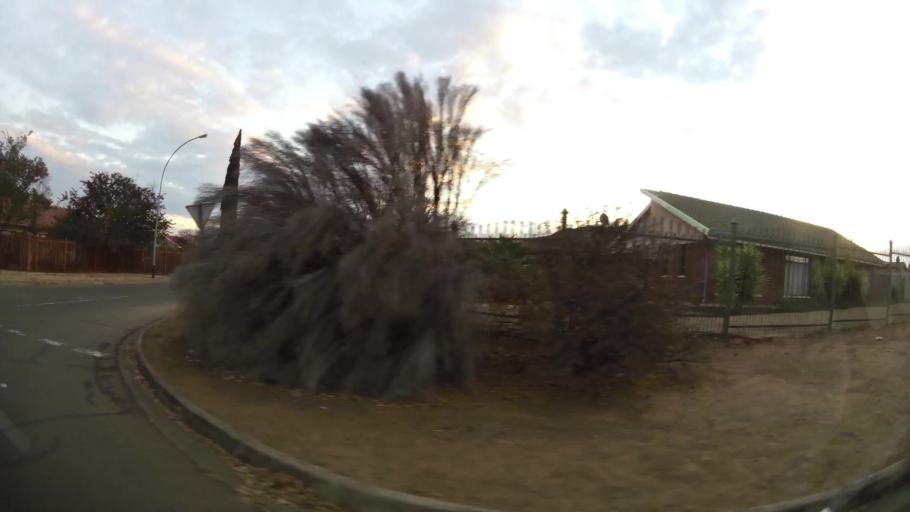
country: ZA
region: Orange Free State
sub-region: Mangaung Metropolitan Municipality
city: Bloemfontein
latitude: -29.1627
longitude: 26.1895
